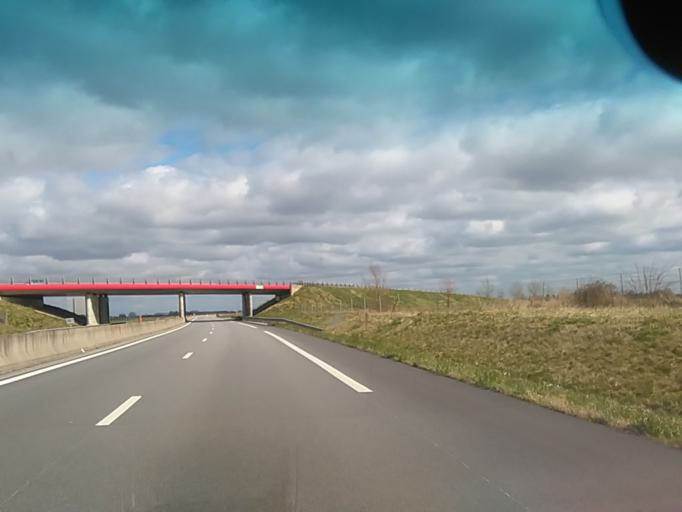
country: FR
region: Haute-Normandie
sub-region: Departement de l'Eure
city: Menneval
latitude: 49.1540
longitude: 0.6296
